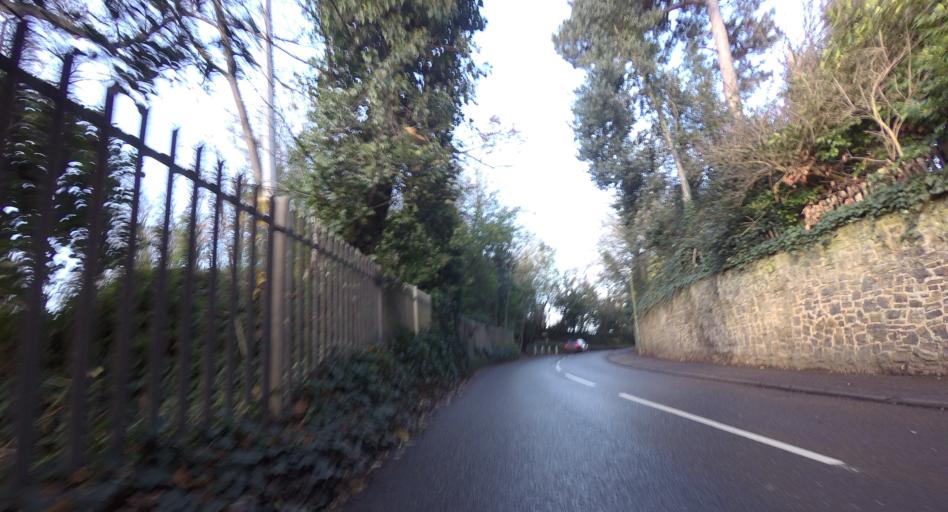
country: GB
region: England
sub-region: Kent
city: Dartford
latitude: 51.4296
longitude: 0.1923
